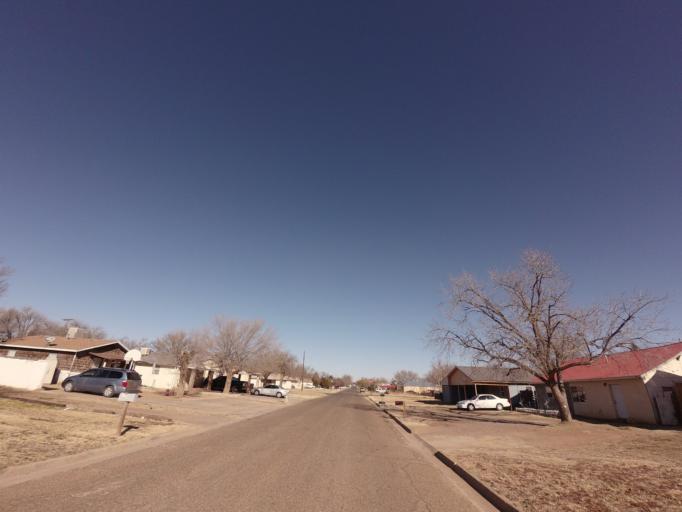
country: US
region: New Mexico
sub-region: Curry County
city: Clovis
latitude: 34.4040
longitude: -103.1940
